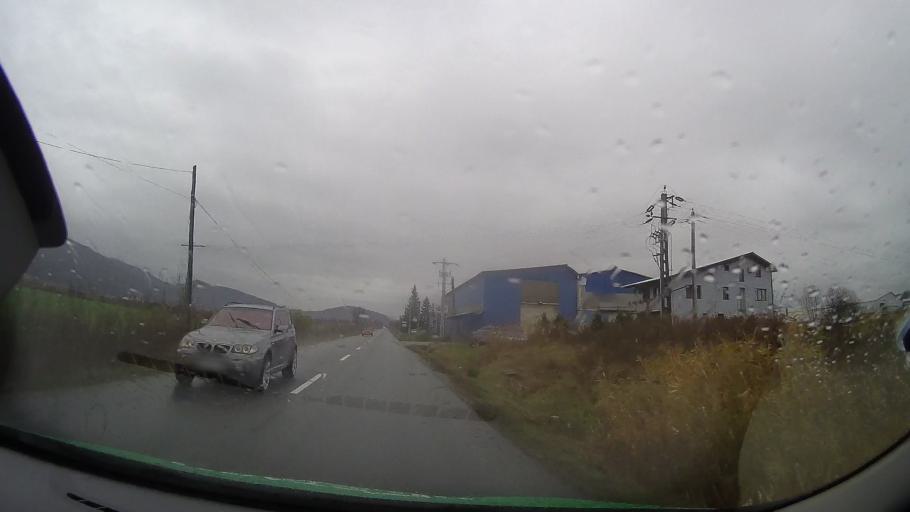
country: RO
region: Bistrita-Nasaud
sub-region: Municipiul Bistrita
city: Viisoara
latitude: 47.0601
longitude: 24.4360
